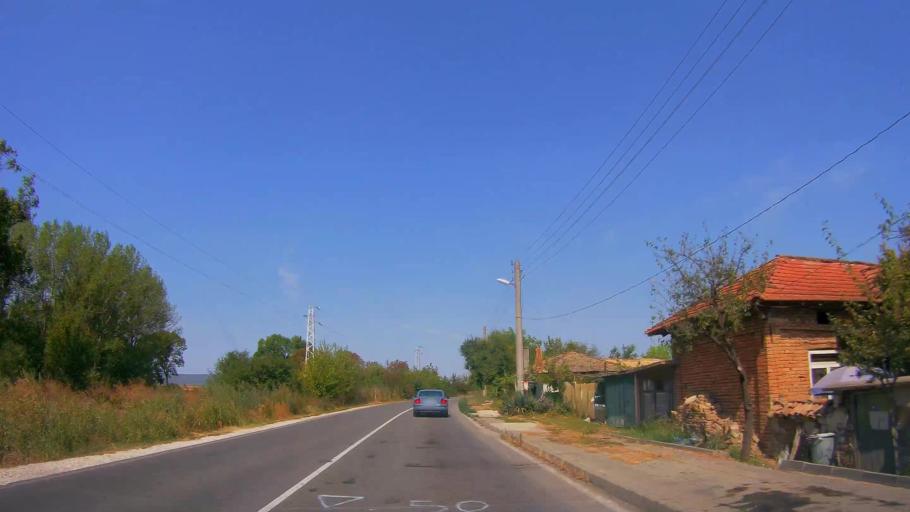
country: BG
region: Shumen
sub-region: Obshtina Smyadovo
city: Smyadovo
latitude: 43.1807
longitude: 27.0063
